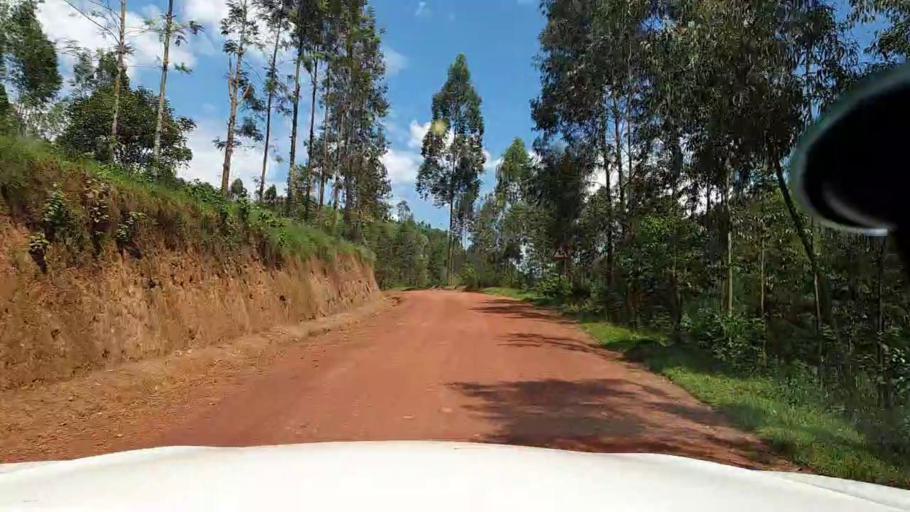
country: RW
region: Northern Province
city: Byumba
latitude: -1.7443
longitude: 29.8630
